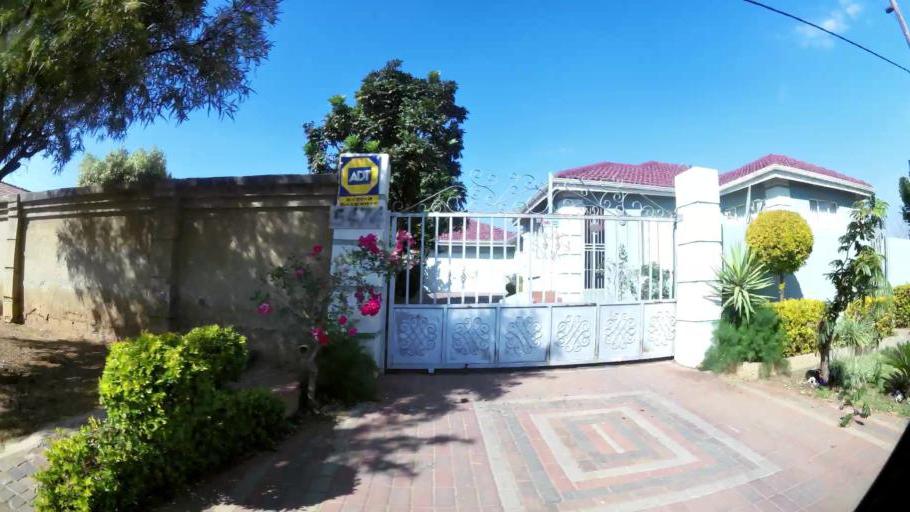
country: ZA
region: Gauteng
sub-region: West Rand District Municipality
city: Muldersdriseloop
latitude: -26.0282
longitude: 27.9394
